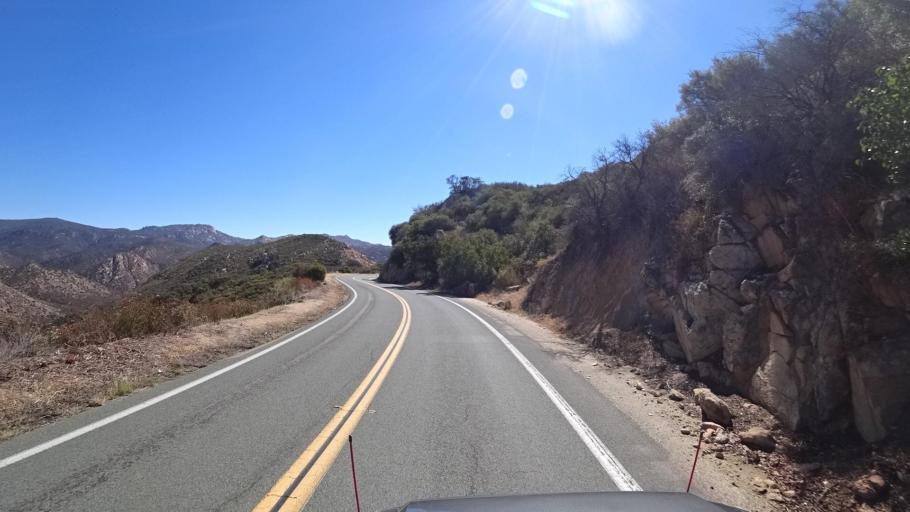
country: US
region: California
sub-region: San Diego County
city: Descanso
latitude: 32.7498
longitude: -116.6678
